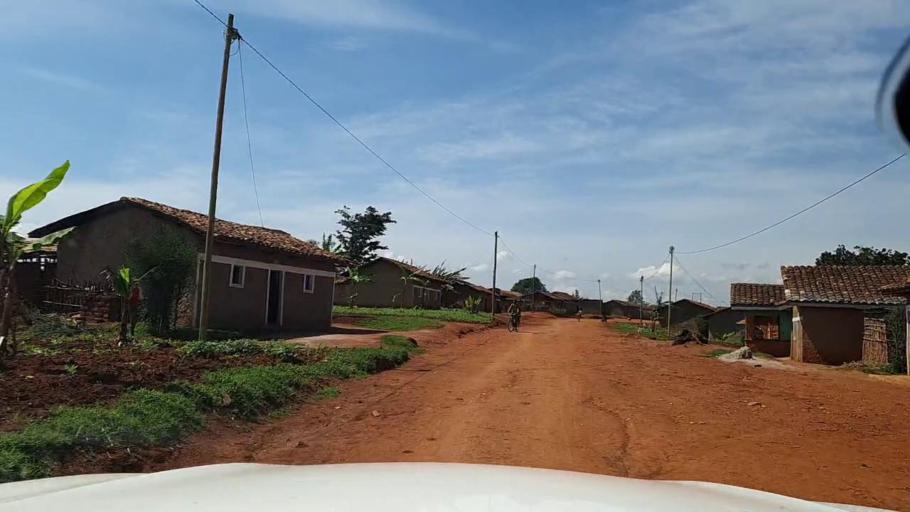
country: RW
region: Southern Province
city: Butare
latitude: -2.7198
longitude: 29.8378
